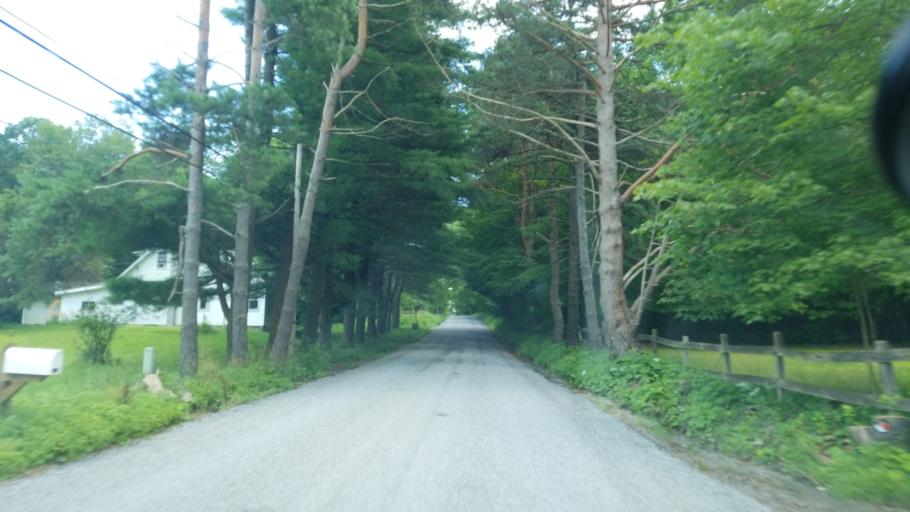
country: US
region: Pennsylvania
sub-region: Jefferson County
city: Brookville
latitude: 41.2301
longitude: -78.9928
